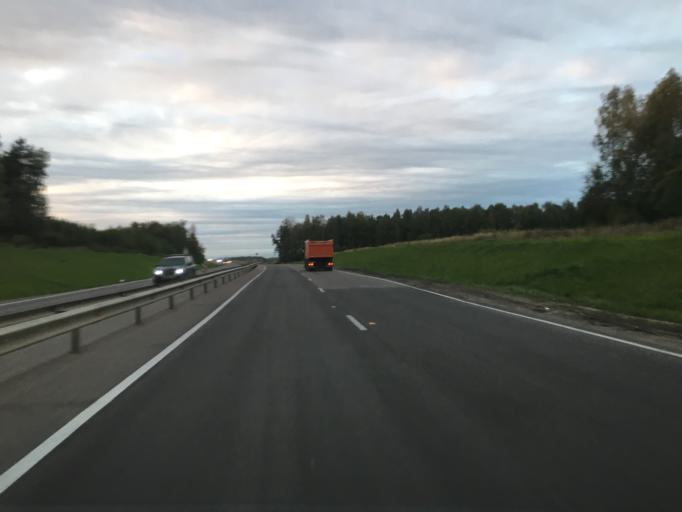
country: RU
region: Kaluga
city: Kaluga
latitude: 54.6096
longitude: 36.3098
